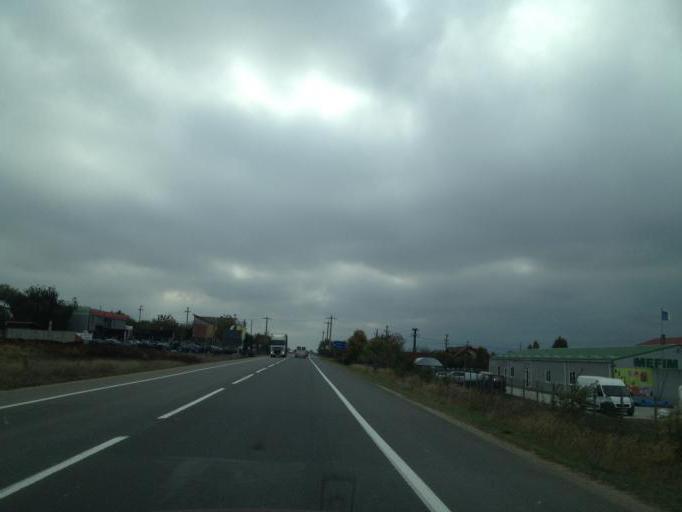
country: RO
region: Dolj
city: Craiova
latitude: 44.3329
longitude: 23.8419
